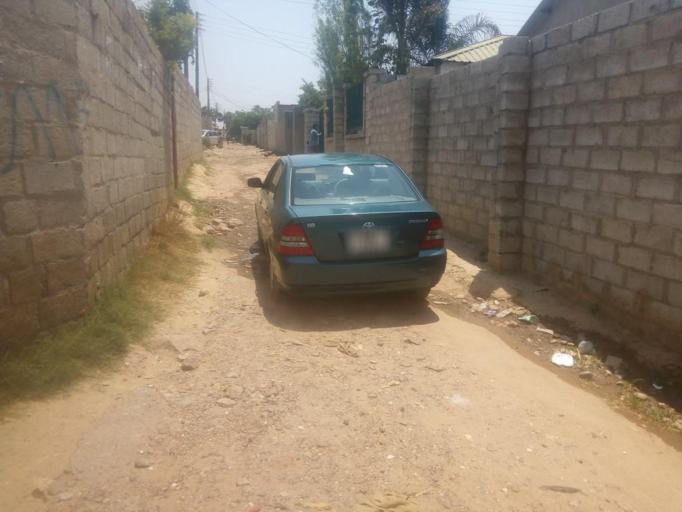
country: ZM
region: Lusaka
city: Lusaka
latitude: -15.4096
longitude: 28.3757
